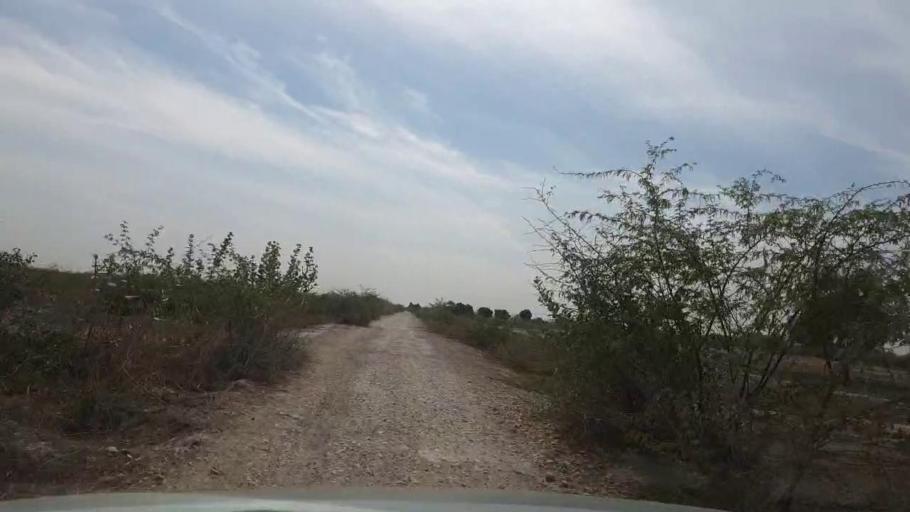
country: PK
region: Sindh
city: Nabisar
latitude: 25.0901
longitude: 69.5998
